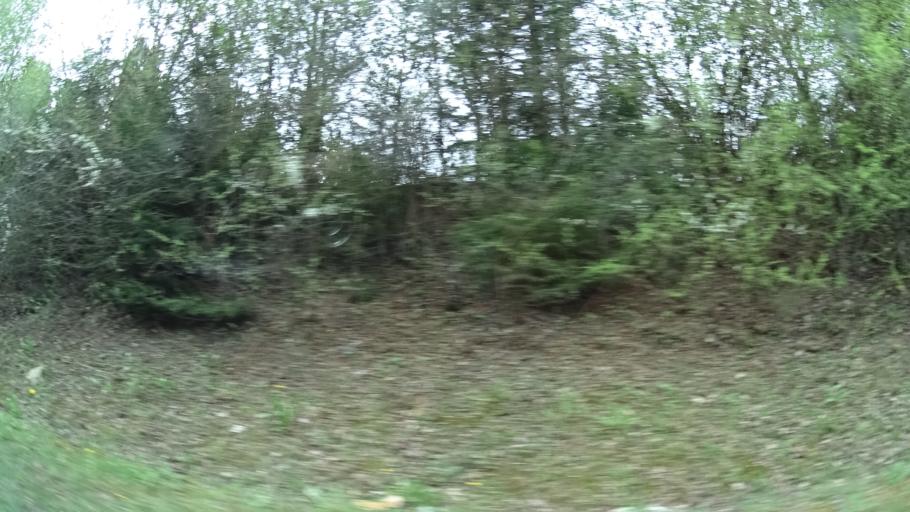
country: DE
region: Baden-Wuerttemberg
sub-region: Freiburg Region
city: Villingen-Schwenningen
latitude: 48.0743
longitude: 8.5035
